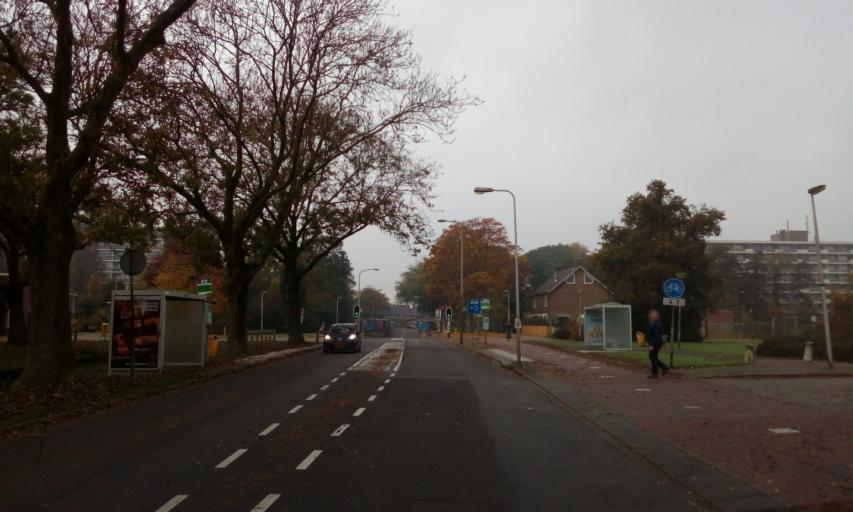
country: NL
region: South Holland
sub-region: Gemeente Waddinxveen
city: Oranjewijk
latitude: 52.0493
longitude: 4.6517
